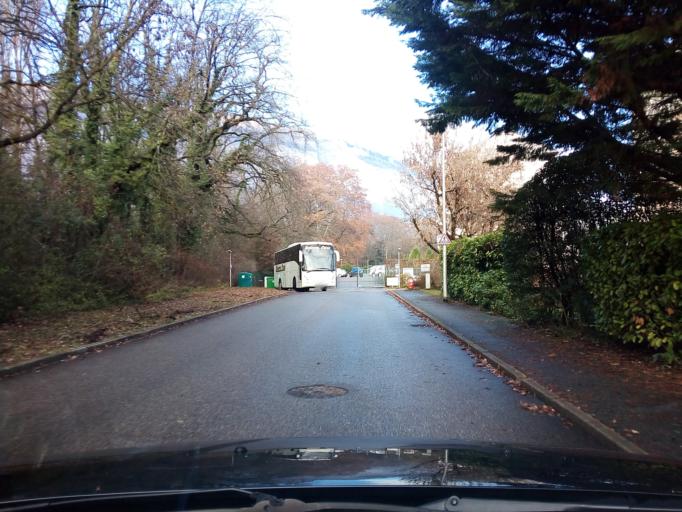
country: FR
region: Rhone-Alpes
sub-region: Departement de l'Isere
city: Meylan
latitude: 45.2126
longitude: 5.7920
